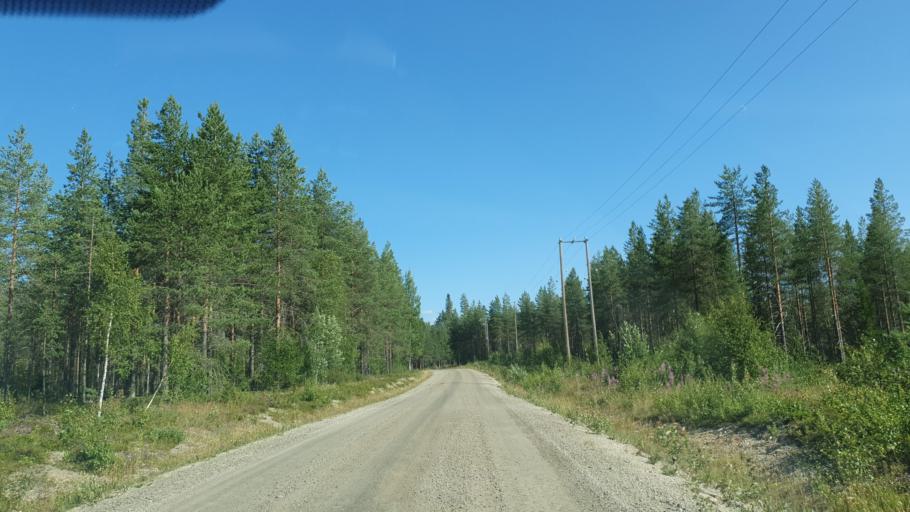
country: FI
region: Kainuu
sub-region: Kehys-Kainuu
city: Kuhmo
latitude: 64.0502
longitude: 29.6058
